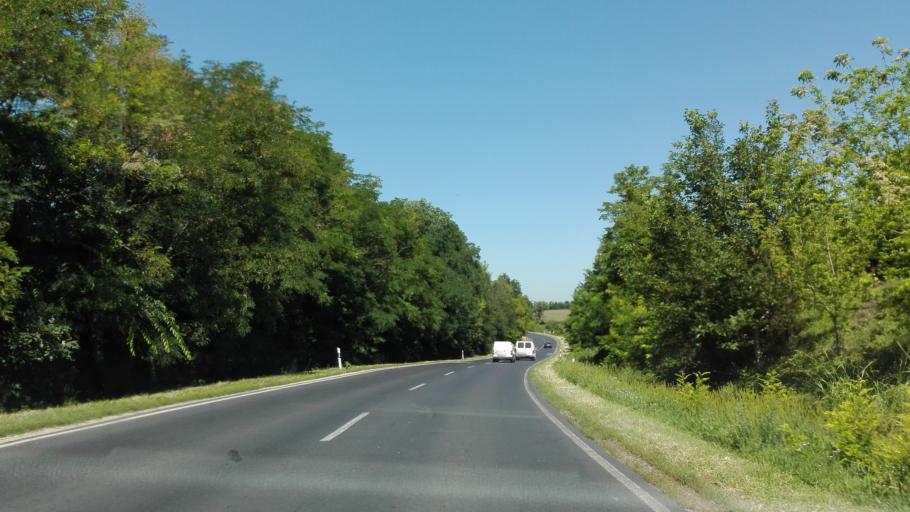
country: HU
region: Fejer
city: Mezoszilas
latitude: 46.7863
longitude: 18.5053
